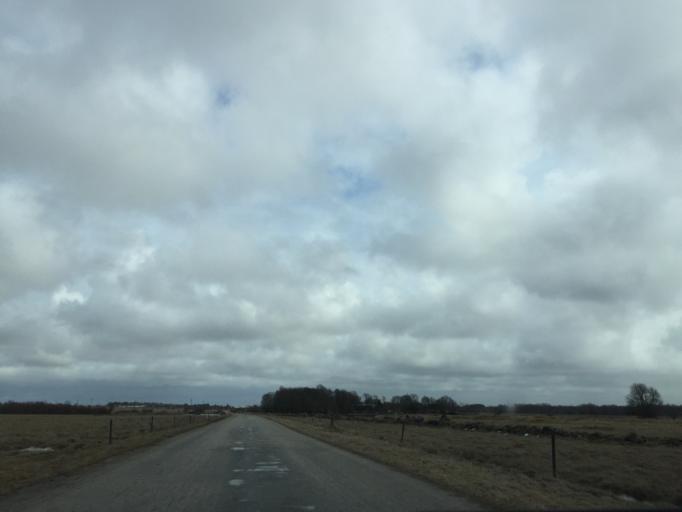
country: EE
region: Laeaene
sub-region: Lihula vald
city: Lihula
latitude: 58.7279
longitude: 23.8926
